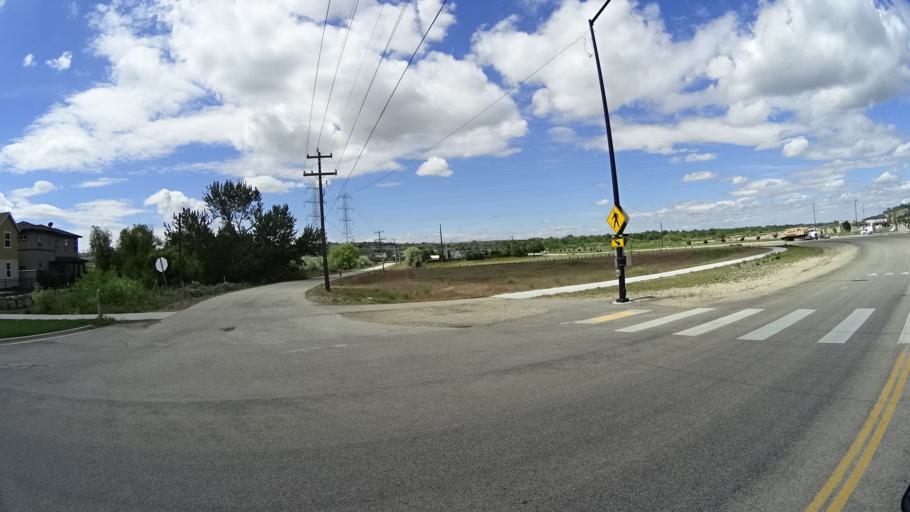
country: US
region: Idaho
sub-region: Ada County
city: Boise
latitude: 43.5709
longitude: -116.1238
